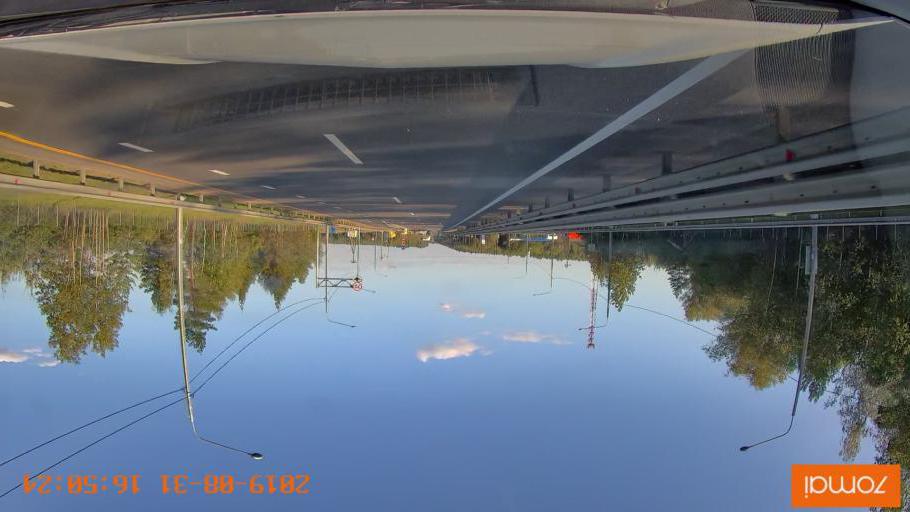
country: RU
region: Kaluga
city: Pyatovskiy
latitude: 54.7079
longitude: 36.1623
